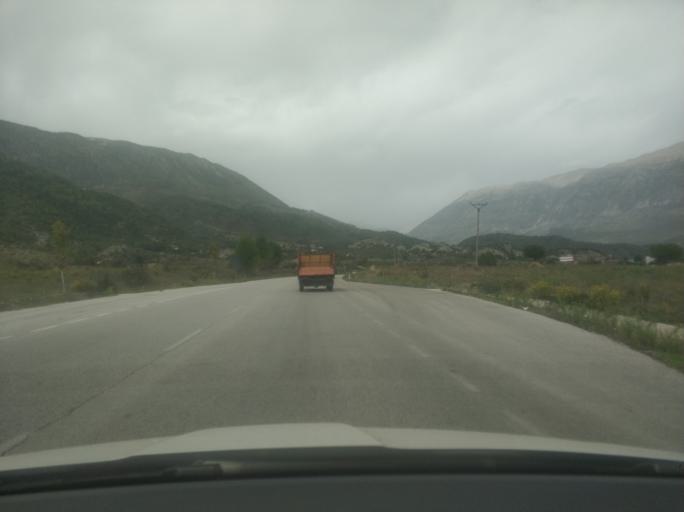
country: AL
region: Gjirokaster
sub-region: Rrethi i Gjirokastres
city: Picar
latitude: 40.1815
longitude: 20.0765
